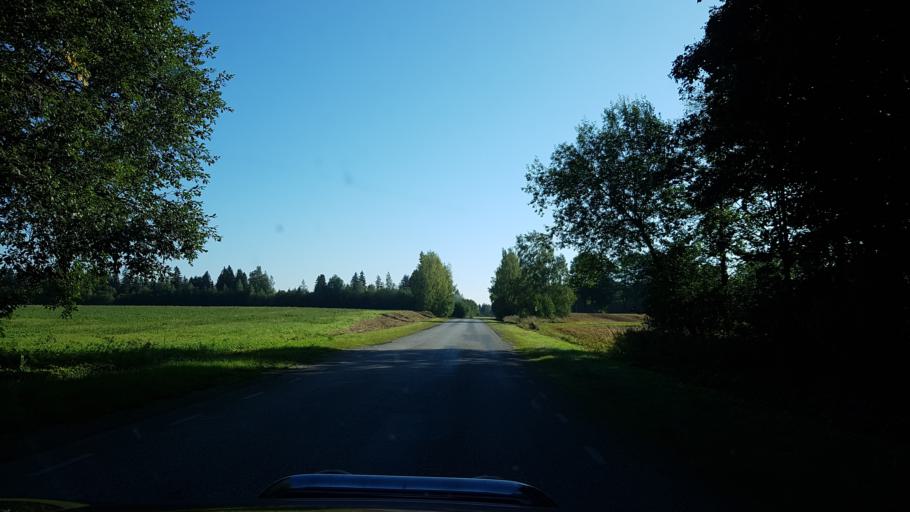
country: EE
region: Jogevamaa
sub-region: Tabivere vald
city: Tabivere
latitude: 58.6799
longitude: 26.6367
